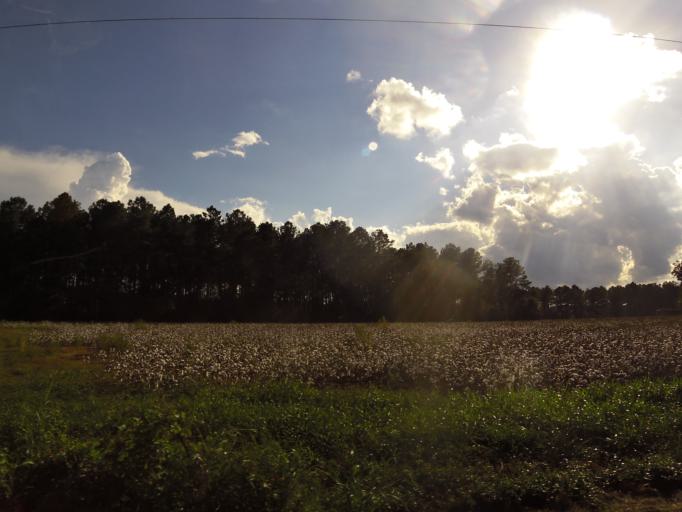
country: US
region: Georgia
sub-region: Brooks County
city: Quitman
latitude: 30.7818
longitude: -83.6207
